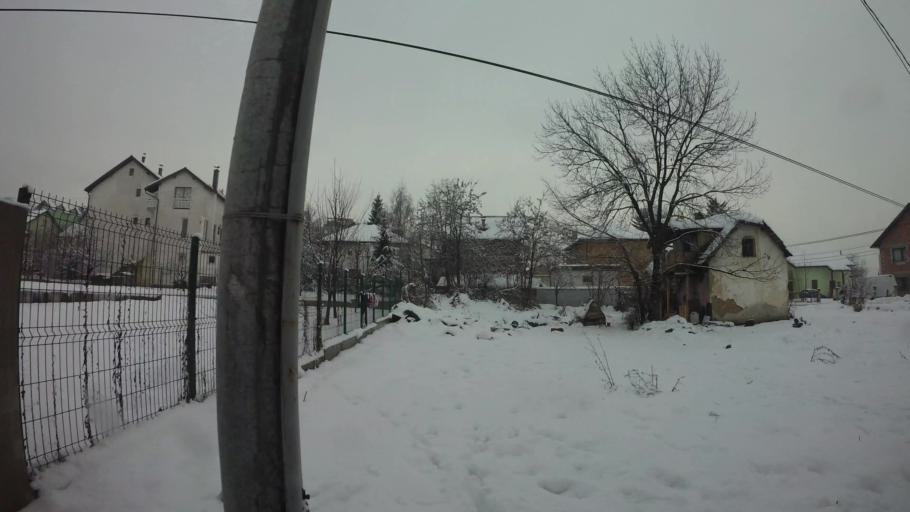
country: BA
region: Federation of Bosnia and Herzegovina
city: Vogosca
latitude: 43.8762
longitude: 18.3154
